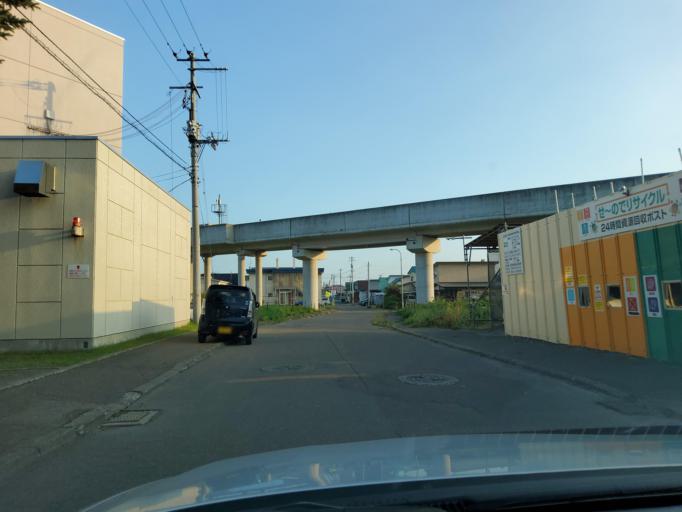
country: JP
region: Hokkaido
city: Obihiro
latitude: 42.9293
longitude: 143.1794
